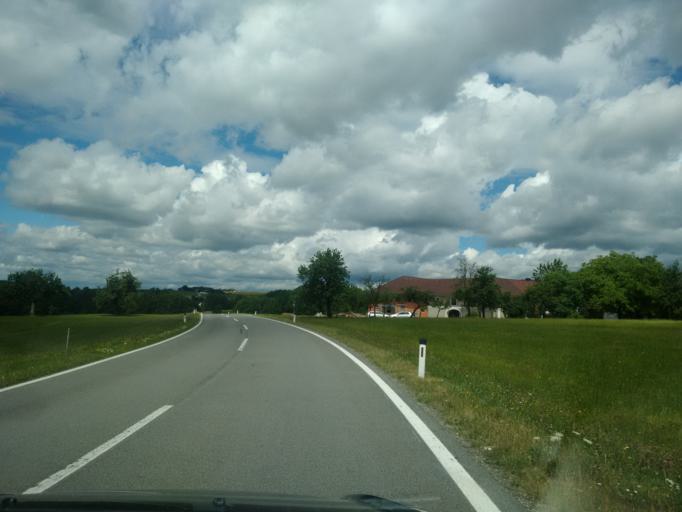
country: AT
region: Upper Austria
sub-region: Politischer Bezirk Urfahr-Umgebung
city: Gramastetten
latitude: 48.4050
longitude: 14.1818
